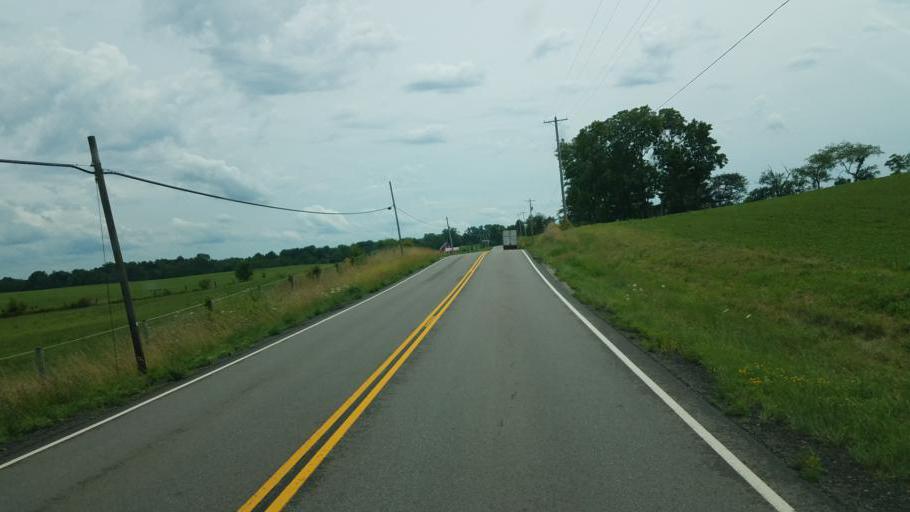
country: US
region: Ohio
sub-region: Knox County
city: Mount Vernon
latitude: 40.3396
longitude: -82.5061
